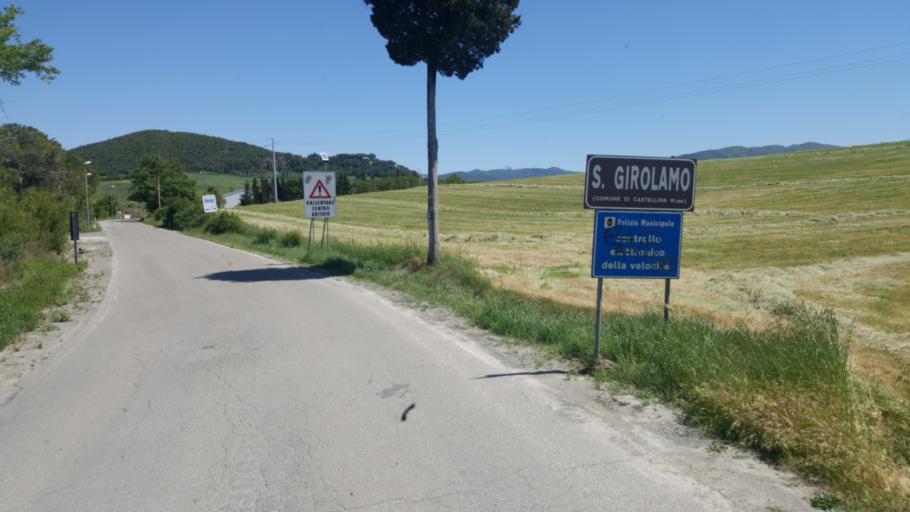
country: IT
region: Tuscany
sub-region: Provincia di Livorno
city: Rosignano Marittimo
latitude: 43.4080
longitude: 10.4965
